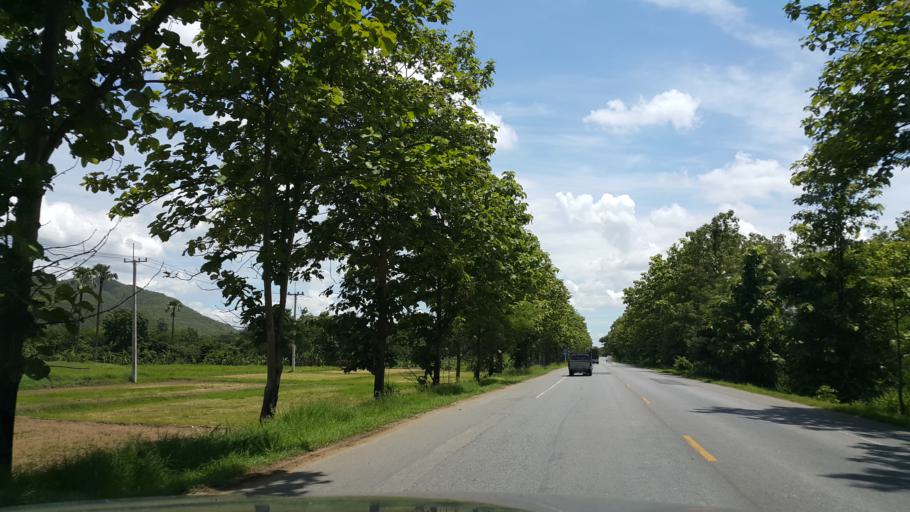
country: TH
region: Chiang Mai
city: Mae On
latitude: 18.7333
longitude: 99.1935
